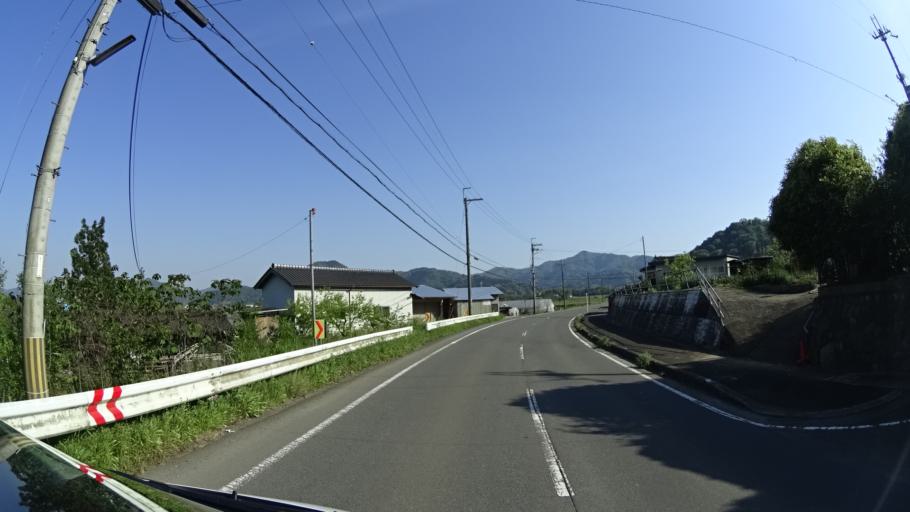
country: JP
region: Kyoto
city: Ayabe
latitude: 35.3182
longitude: 135.2099
